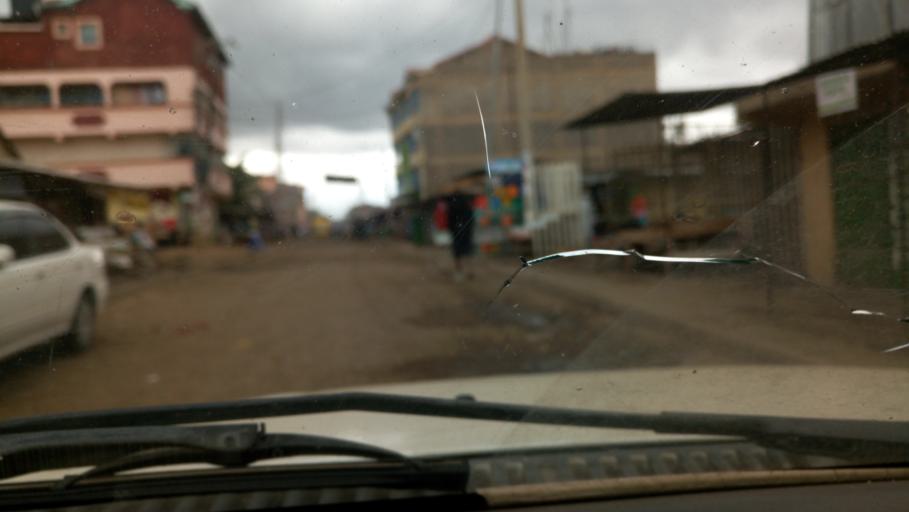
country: KE
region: Nairobi Area
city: Pumwani
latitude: -1.2302
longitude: 36.9270
